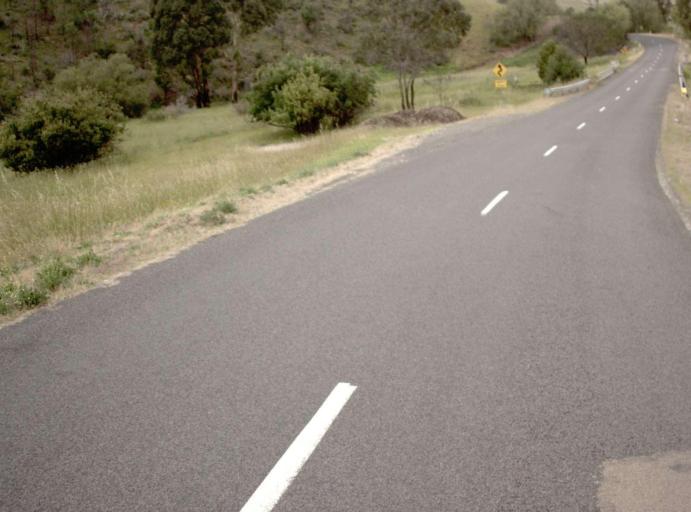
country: AU
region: Victoria
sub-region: Wellington
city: Heyfield
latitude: -37.8534
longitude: 146.7072
